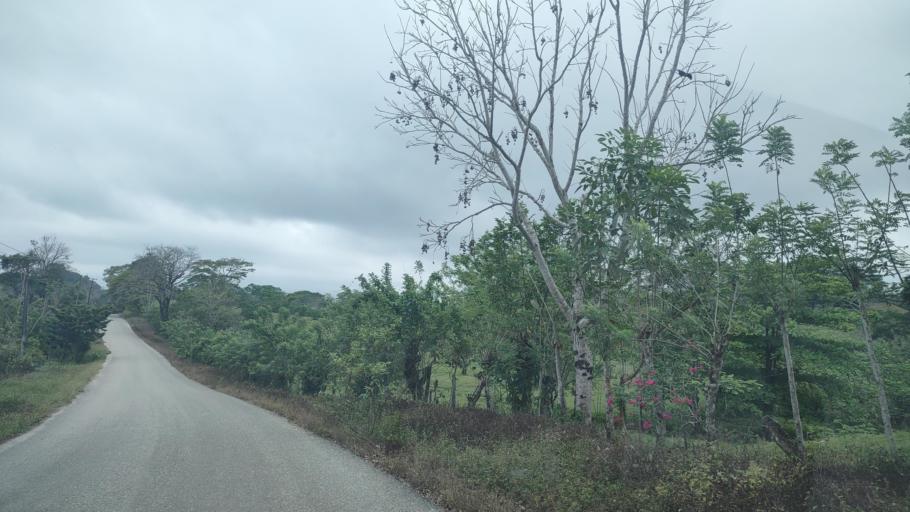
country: MX
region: Veracruz
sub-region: Uxpanapa
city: Poblado 10
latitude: 17.4797
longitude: -94.1199
